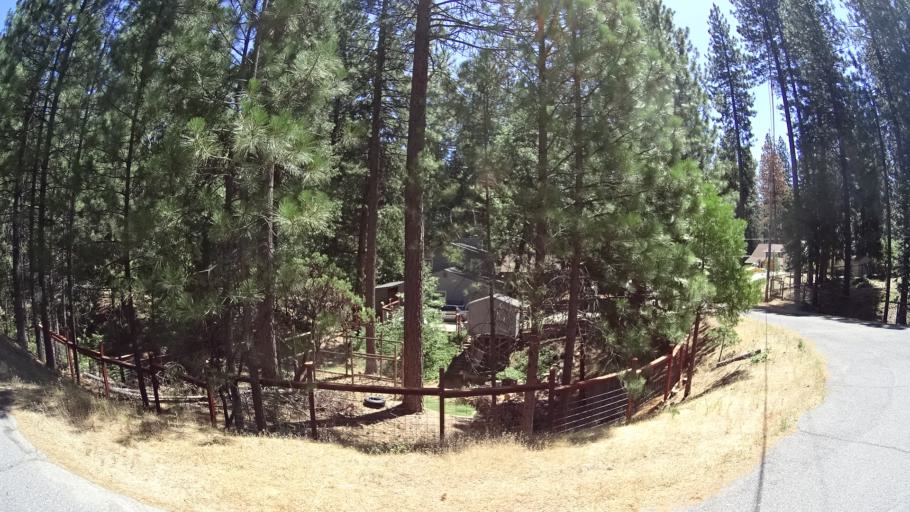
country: US
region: California
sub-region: Calaveras County
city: Arnold
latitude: 38.2282
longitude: -120.3419
